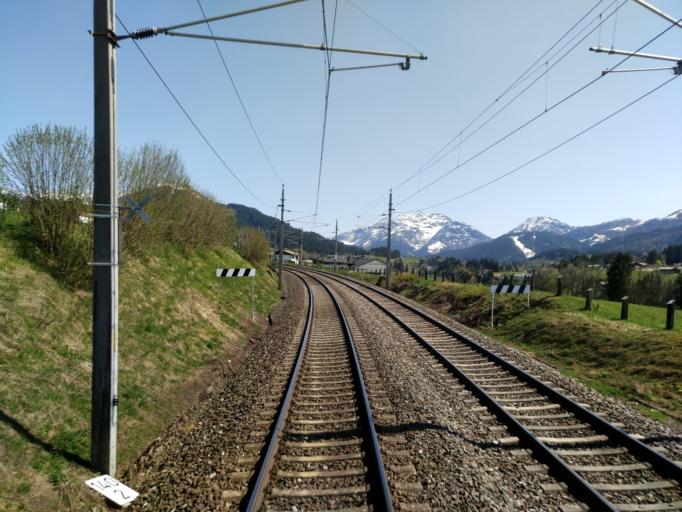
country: AT
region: Tyrol
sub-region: Politischer Bezirk Kitzbuhel
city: Fieberbrunn
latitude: 47.4935
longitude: 12.5188
